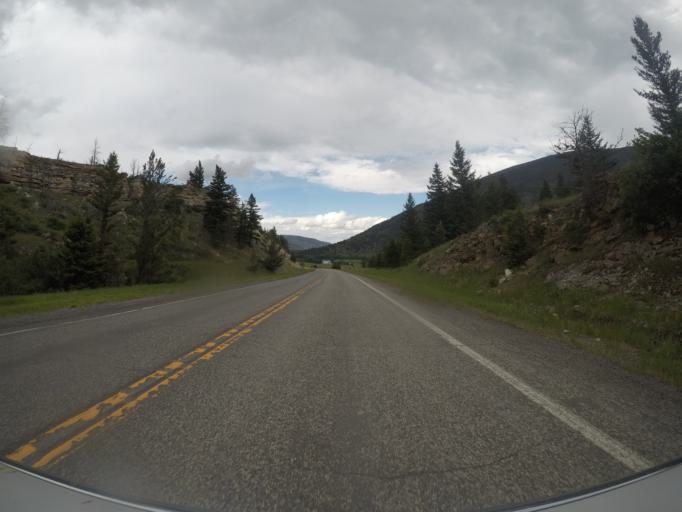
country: US
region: Montana
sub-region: Park County
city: Livingston
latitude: 45.5518
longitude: -110.2063
